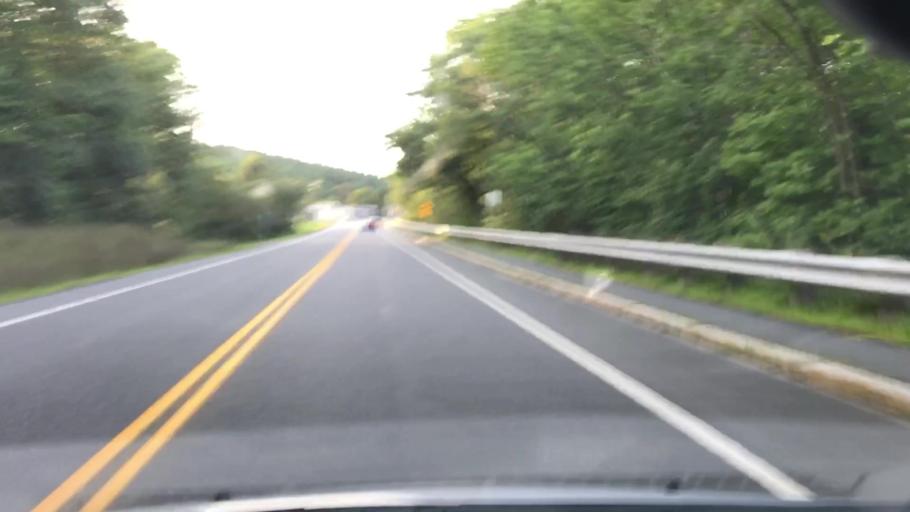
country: US
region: New Hampshire
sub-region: Grafton County
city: Rumney
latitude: 43.9236
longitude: -71.8904
